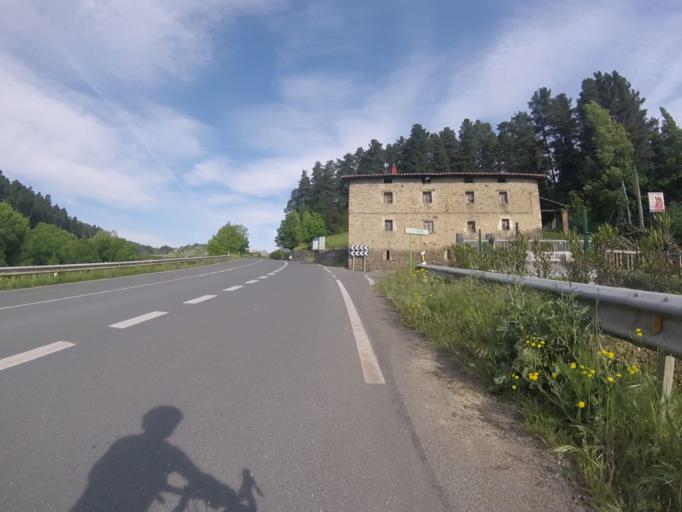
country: ES
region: Basque Country
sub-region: Provincia de Guipuzcoa
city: Zumarraga
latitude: 43.0812
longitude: -2.2982
